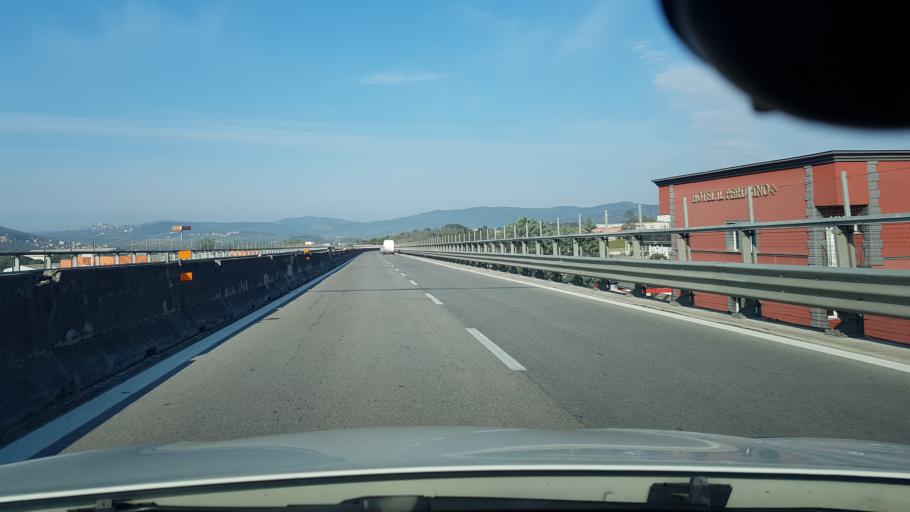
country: IT
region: Umbria
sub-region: Provincia di Perugia
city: Chiugiana-La Commenda
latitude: 43.1013
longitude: 12.3106
